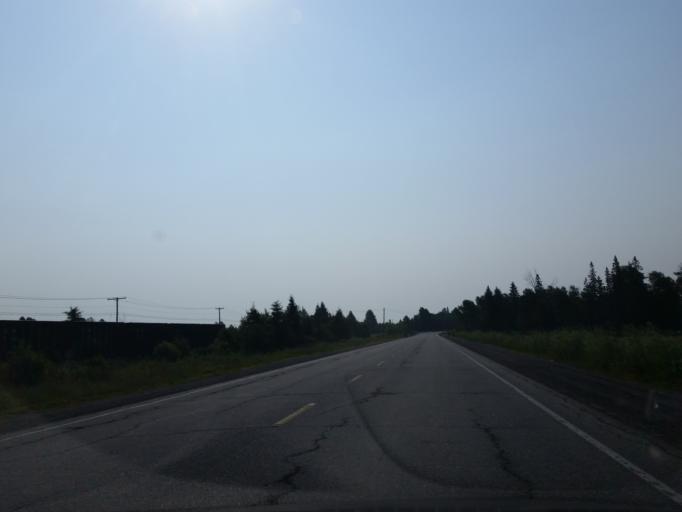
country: CA
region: Ontario
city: Greater Sudbury
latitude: 46.4378
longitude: -80.2874
